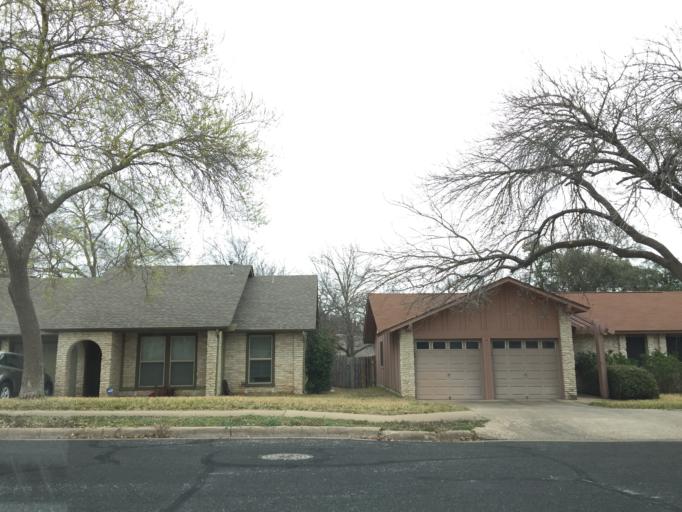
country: US
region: Texas
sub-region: Williamson County
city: Jollyville
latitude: 30.4149
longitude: -97.7406
